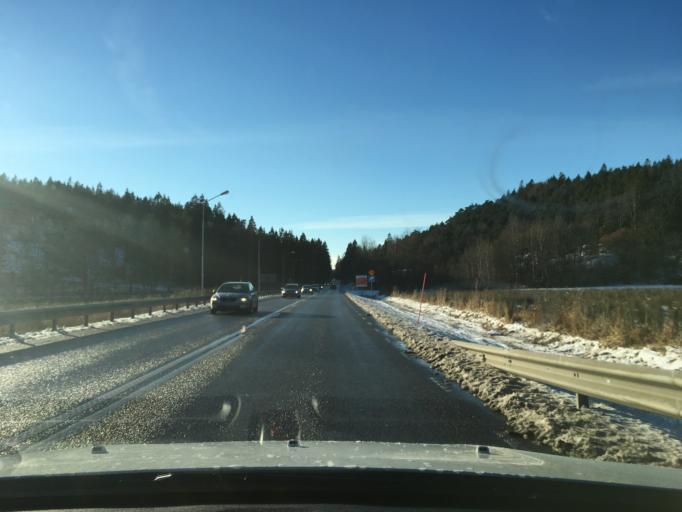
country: SE
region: Vaestra Goetaland
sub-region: Tjorns Kommun
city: Myggenas
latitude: 58.1227
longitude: 11.7192
